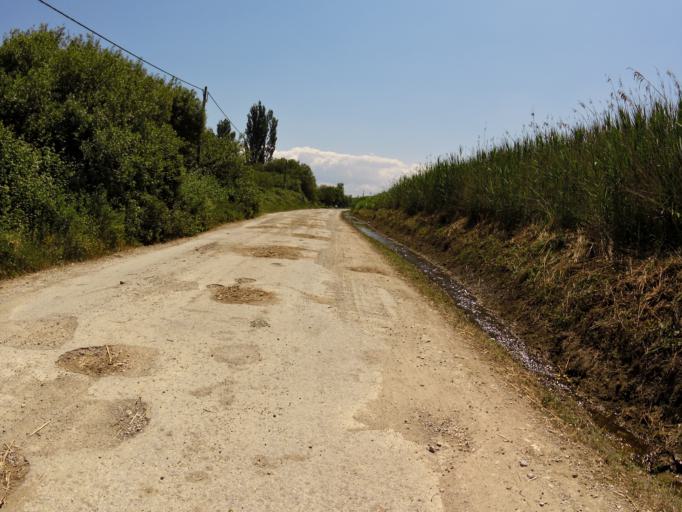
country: PT
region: Coimbra
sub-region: Montemor-O-Velho
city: Montemor-o-Velho
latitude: 40.1486
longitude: -8.7169
